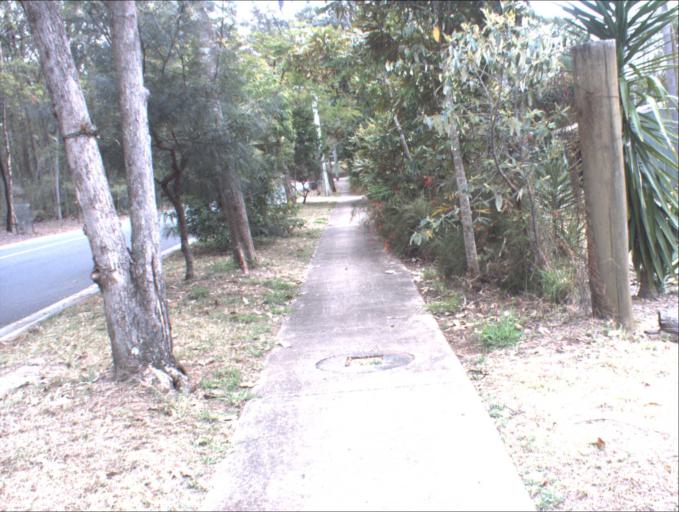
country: AU
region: Queensland
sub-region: Logan
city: Slacks Creek
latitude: -27.6684
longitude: 153.1681
